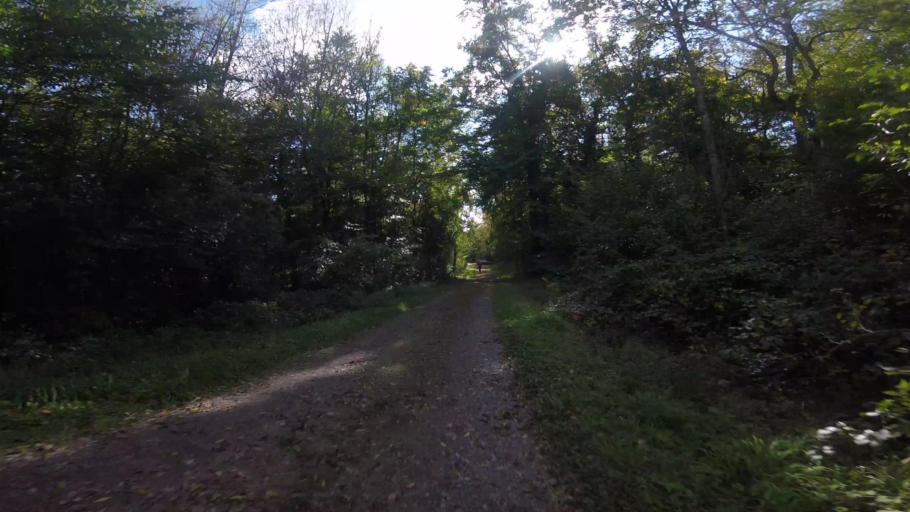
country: DE
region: Baden-Wuerttemberg
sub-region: Regierungsbezirk Stuttgart
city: Kirchberg an der Murr
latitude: 48.9845
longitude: 9.3358
